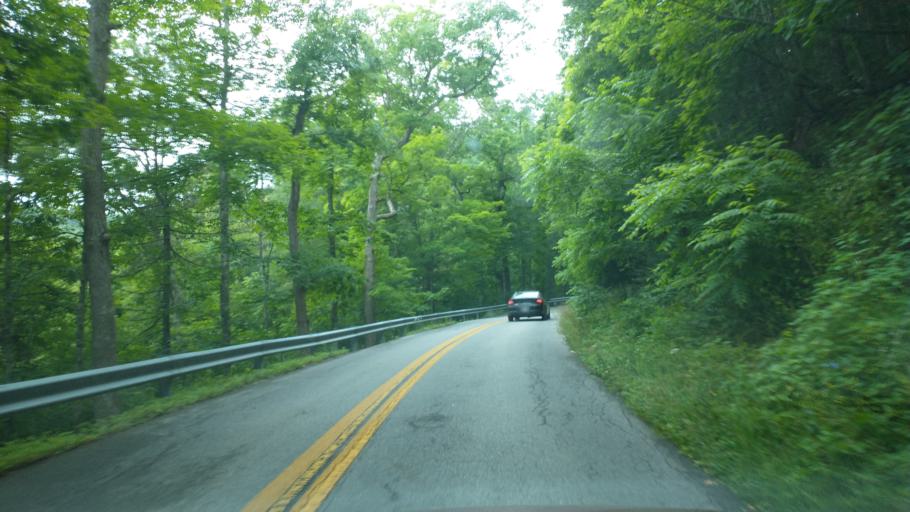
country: US
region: West Virginia
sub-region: Mercer County
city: Athens
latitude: 37.4241
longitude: -81.0015
